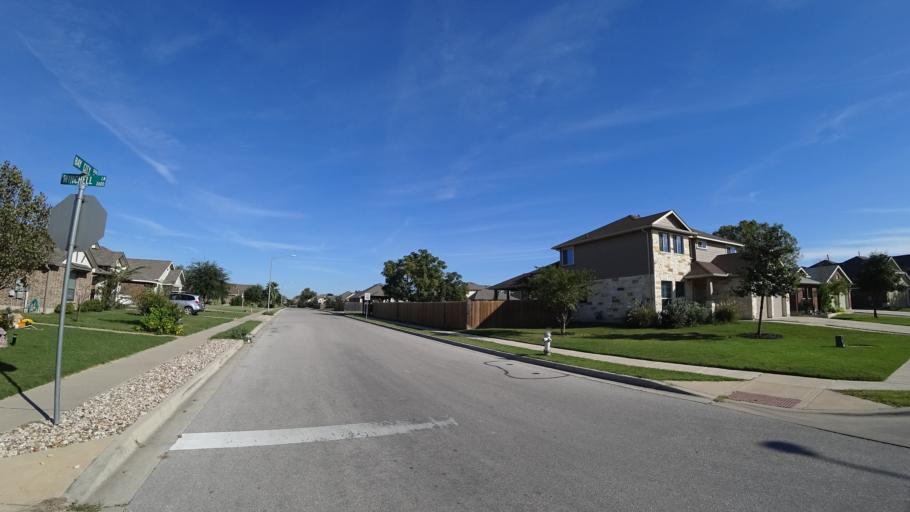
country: US
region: Texas
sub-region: Travis County
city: Austin
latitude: 30.2616
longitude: -97.6712
